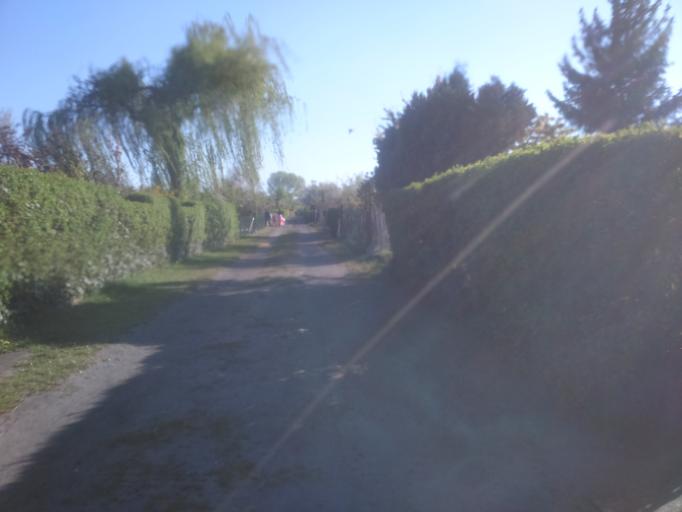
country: DE
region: Berlin
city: Neu-Hohenschoenhausen
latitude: 52.5588
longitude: 13.5085
